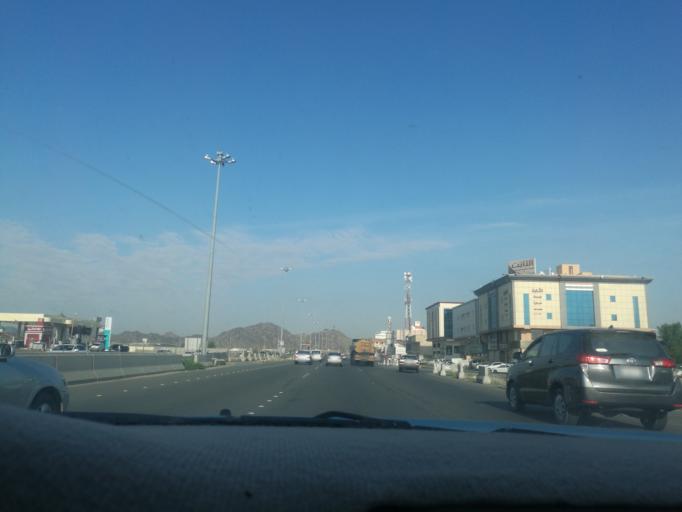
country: SA
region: Makkah
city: Al Jumum
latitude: 21.5742
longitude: 39.7672
